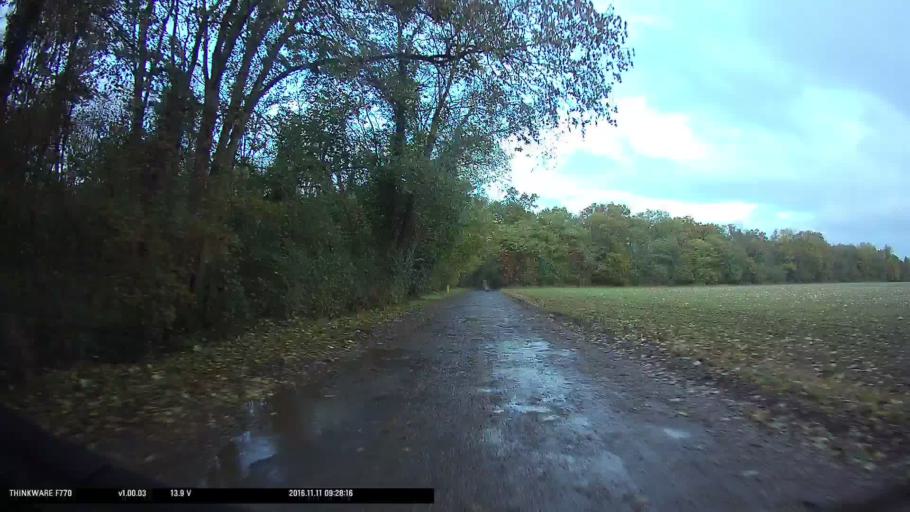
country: FR
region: Ile-de-France
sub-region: Departement du Val-d'Oise
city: Osny
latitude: 49.0712
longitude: 2.0417
